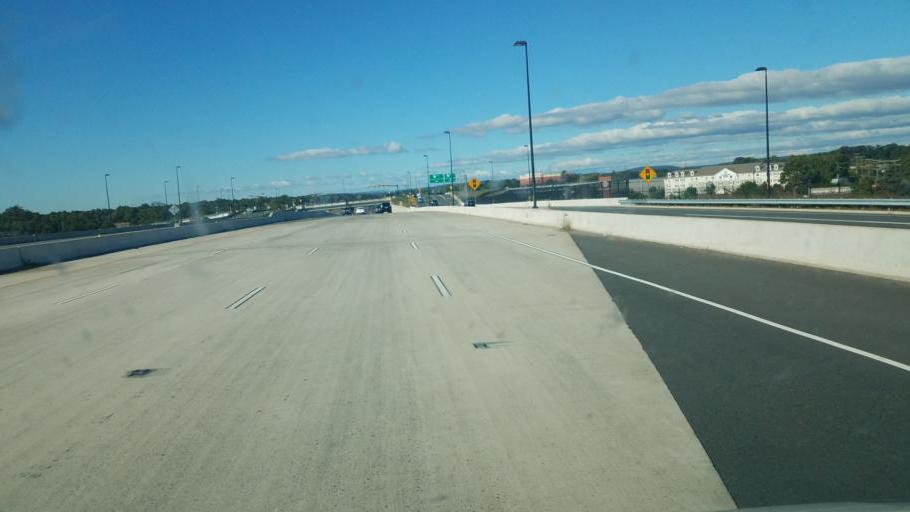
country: US
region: Virginia
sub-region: Prince William County
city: Gainesville
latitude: 38.7972
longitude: -77.6088
